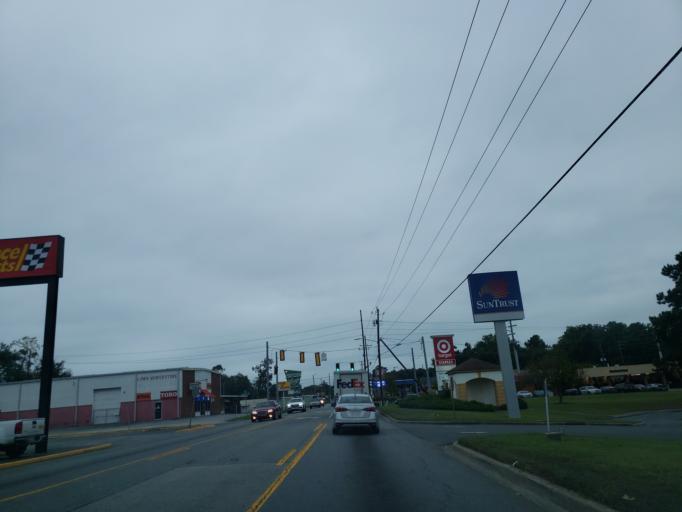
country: US
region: Georgia
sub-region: Chatham County
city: Thunderbolt
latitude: 32.0394
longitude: -81.0652
